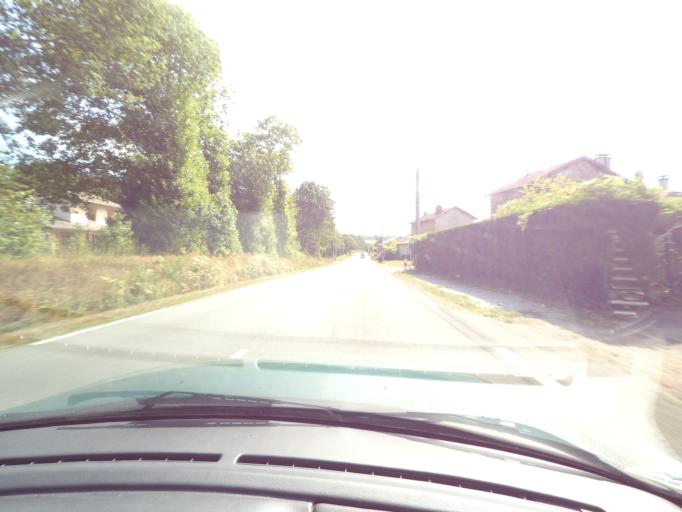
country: FR
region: Limousin
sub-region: Departement de la Haute-Vienne
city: Feytiat
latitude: 45.8080
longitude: 1.3521
